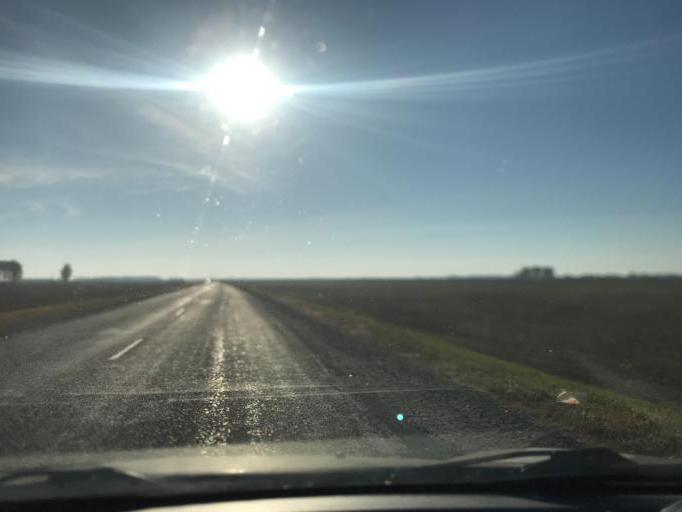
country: BY
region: Gomel
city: Khoyniki
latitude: 51.8387
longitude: 30.0400
